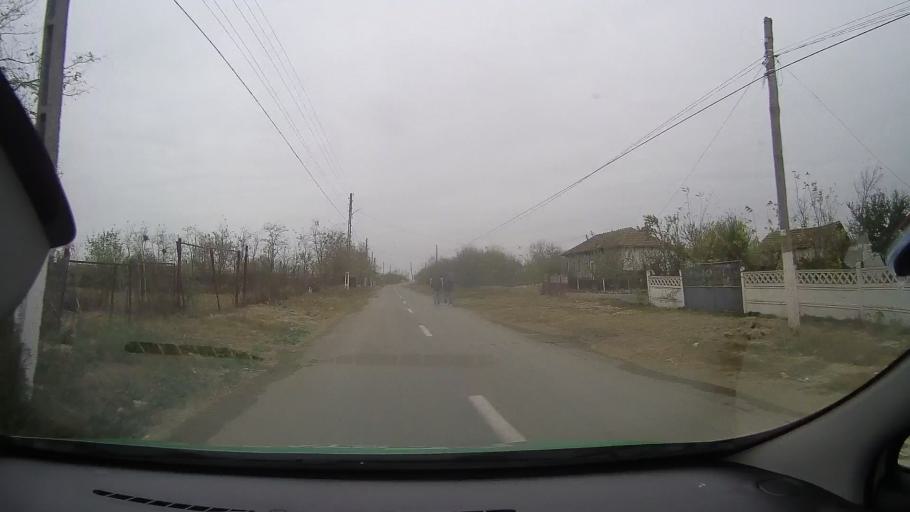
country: RO
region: Constanta
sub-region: Comuna Vulturu
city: Vulturu
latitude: 44.6497
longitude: 28.2687
